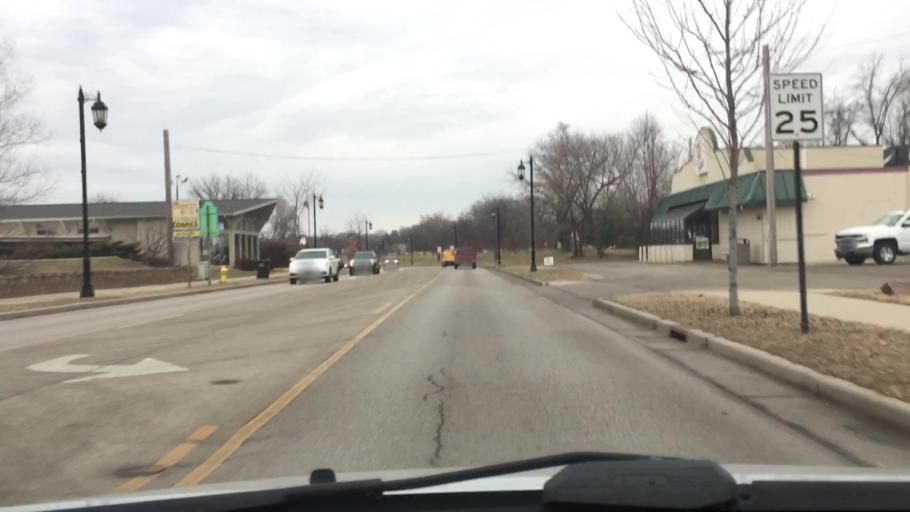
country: US
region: Wisconsin
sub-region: Waukesha County
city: Oconomowoc
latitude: 43.1082
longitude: -88.4911
